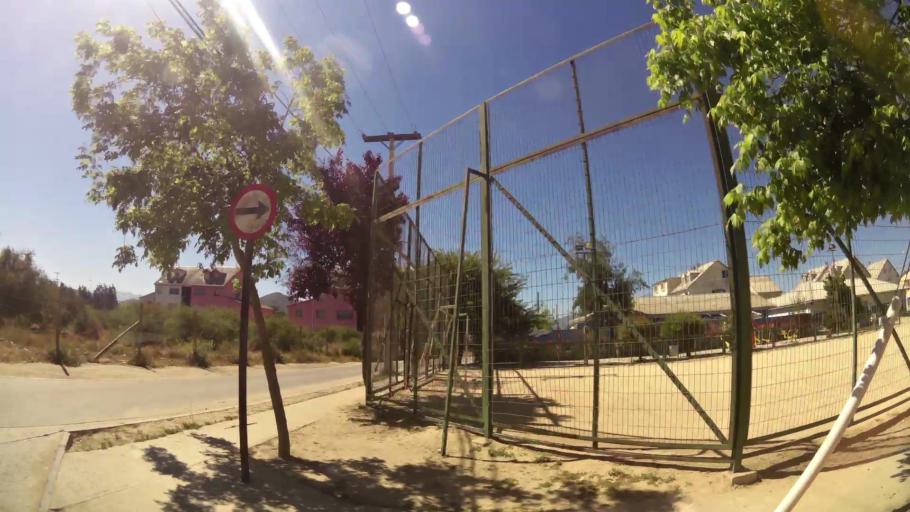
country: CL
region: Valparaiso
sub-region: Provincia de Marga Marga
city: Quilpue
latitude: -33.3045
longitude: -71.4139
